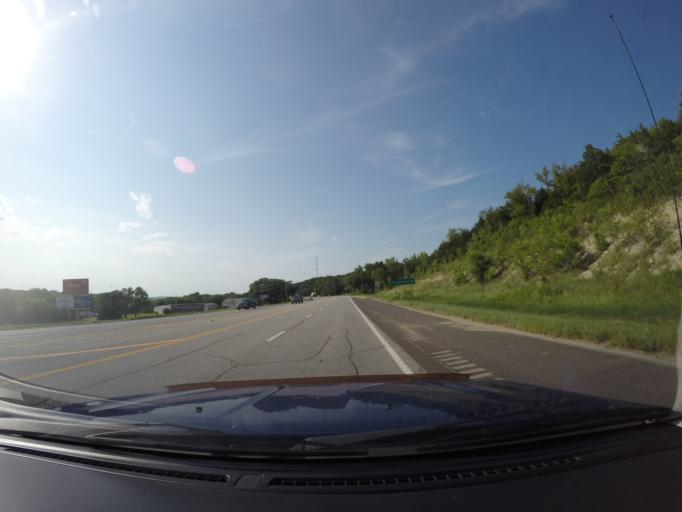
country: US
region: Kansas
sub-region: Riley County
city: Manhattan
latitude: 39.1662
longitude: -96.5404
